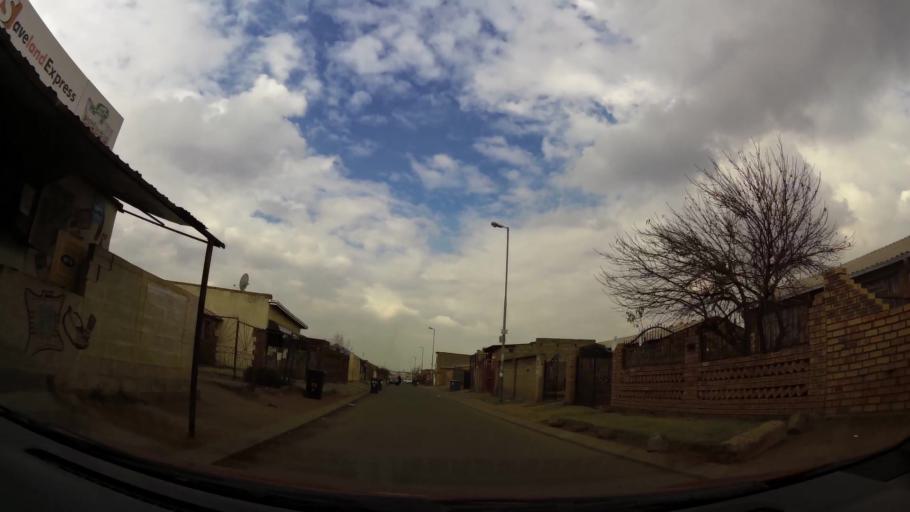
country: ZA
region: Gauteng
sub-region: City of Johannesburg Metropolitan Municipality
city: Soweto
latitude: -26.2521
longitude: 27.8323
